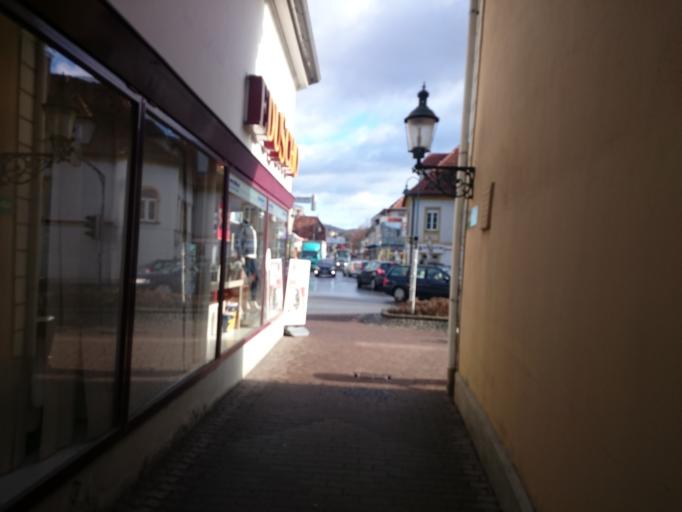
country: AT
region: Styria
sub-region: Politischer Bezirk Weiz
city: Weiz
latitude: 47.2168
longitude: 15.6263
